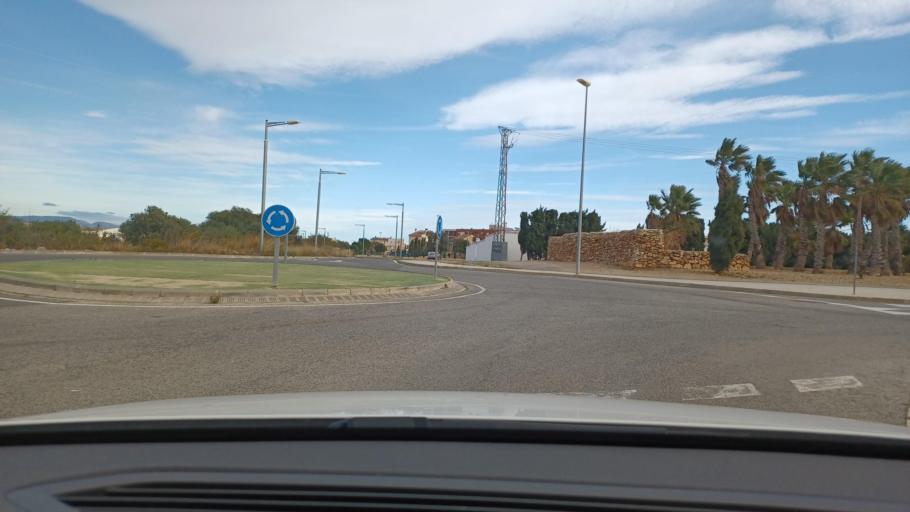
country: ES
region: Catalonia
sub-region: Provincia de Tarragona
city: Amposta
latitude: 40.7106
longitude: 0.5675
